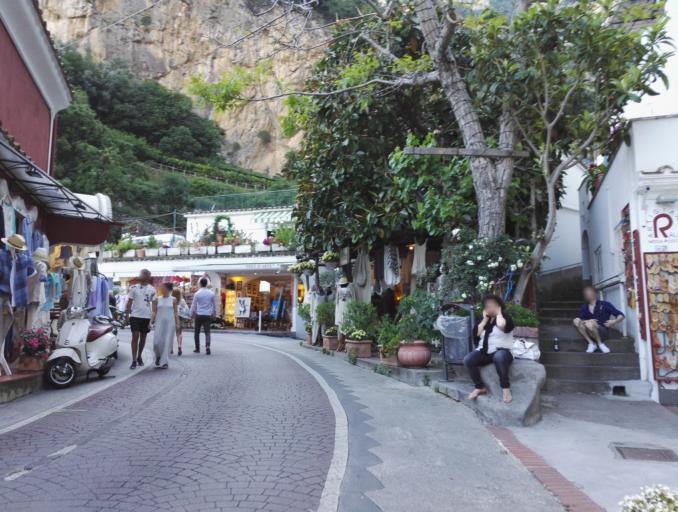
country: IT
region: Campania
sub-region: Provincia di Salerno
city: Positano
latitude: 40.6309
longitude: 14.4851
